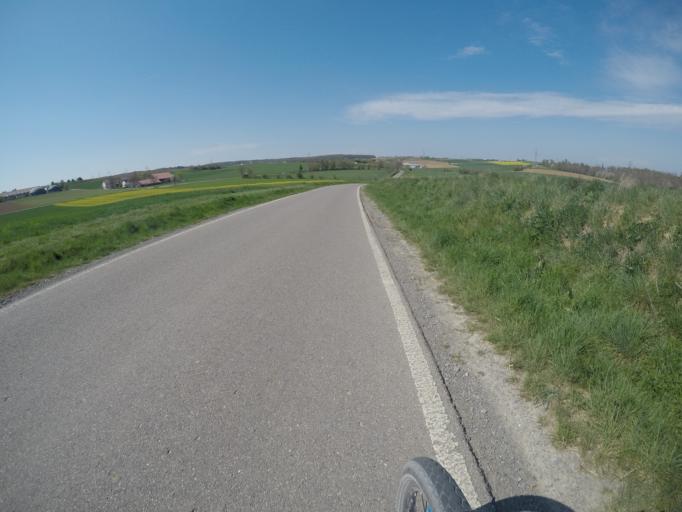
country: DE
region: Baden-Wuerttemberg
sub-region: Regierungsbezirk Stuttgart
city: Hemmingen
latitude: 48.8428
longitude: 9.0138
